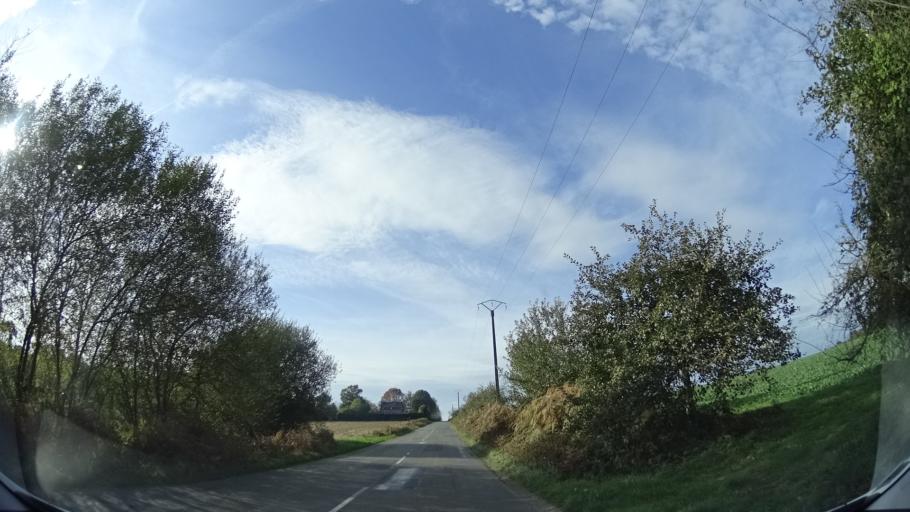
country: FR
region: Brittany
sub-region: Departement d'Ille-et-Vilaine
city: Geveze
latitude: 48.2162
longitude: -1.8386
